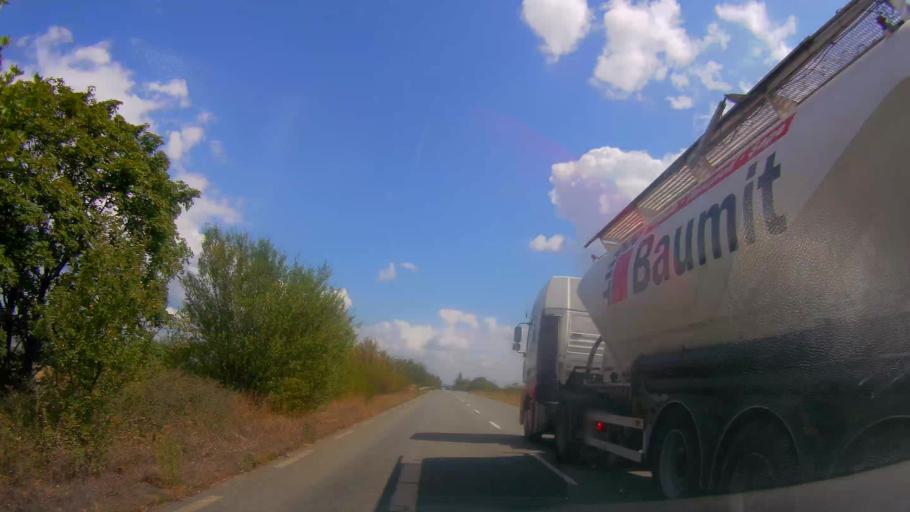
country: BG
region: Sliven
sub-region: Obshtina Tvurditsa
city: Tvurditsa
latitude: 42.6563
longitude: 25.9304
